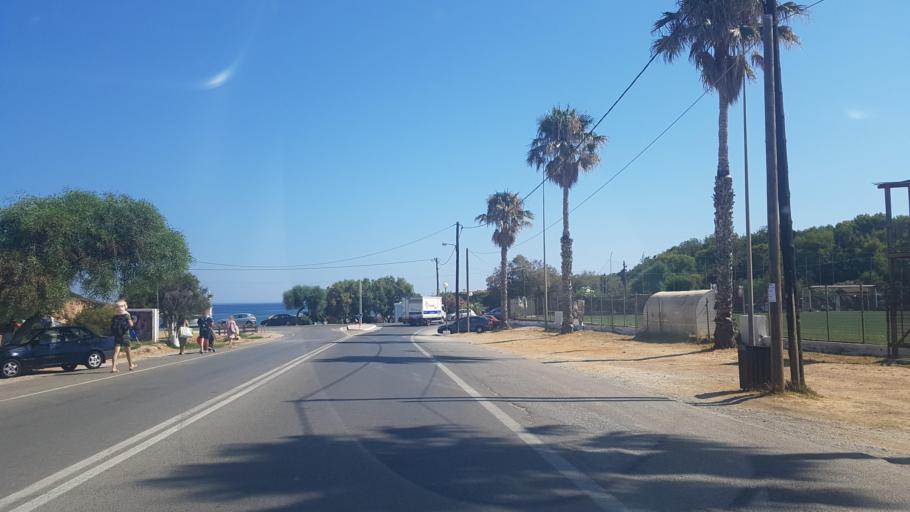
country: GR
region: Crete
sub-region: Nomos Chanias
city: Daratsos
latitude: 35.5129
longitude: 23.9833
